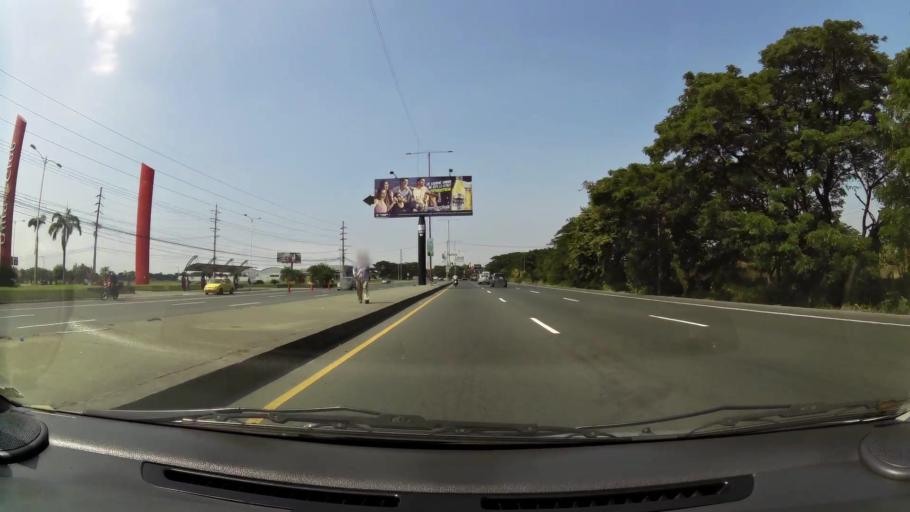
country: EC
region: Guayas
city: Eloy Alfaro
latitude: -2.0511
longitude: -79.8898
